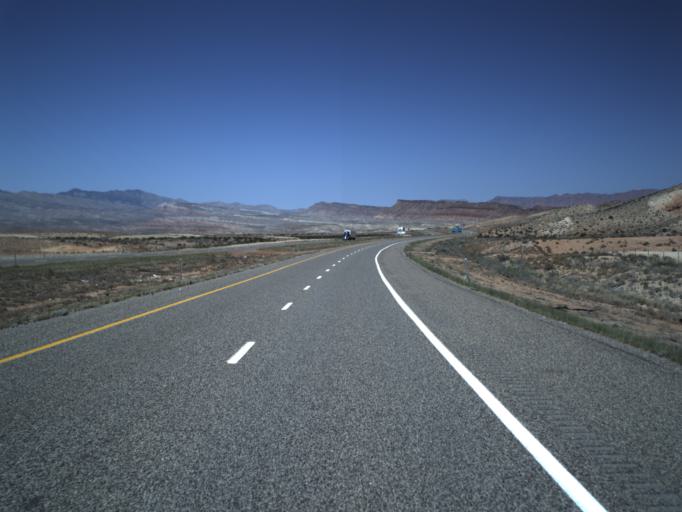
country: US
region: Utah
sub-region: Washington County
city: Saint George
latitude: 37.0074
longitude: -113.5874
